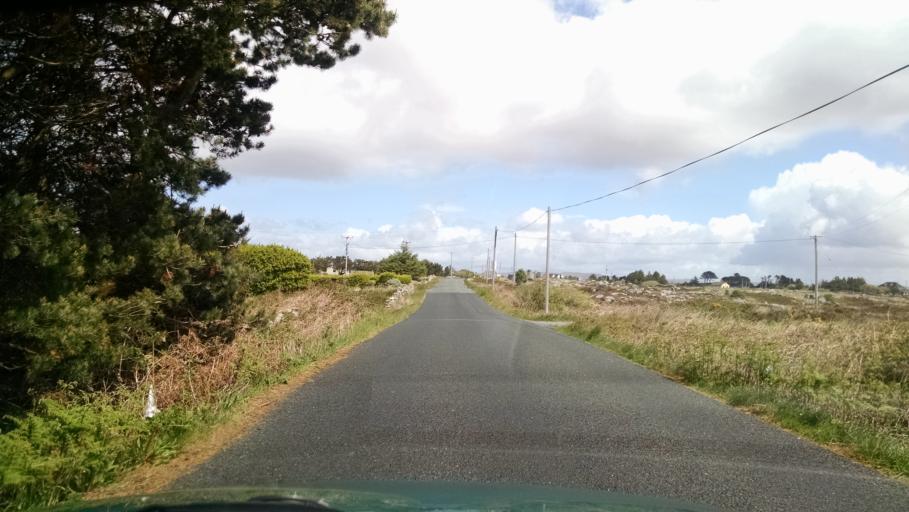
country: IE
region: Connaught
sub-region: County Galway
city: Oughterard
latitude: 53.2976
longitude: -9.5802
